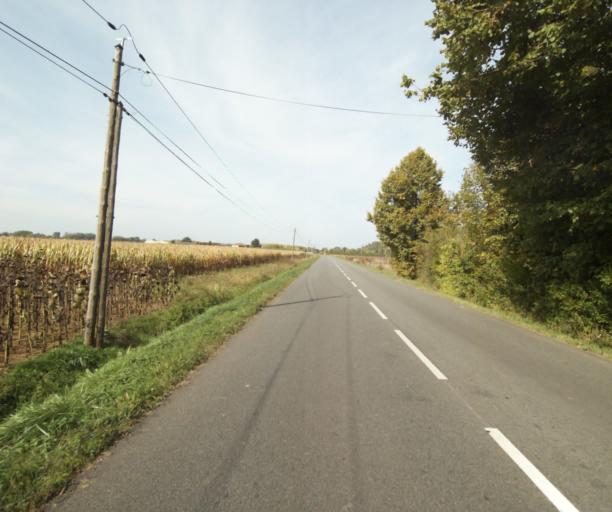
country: FR
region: Midi-Pyrenees
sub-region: Departement du Tarn-et-Garonne
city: Corbarieu
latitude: 43.9326
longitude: 1.3812
